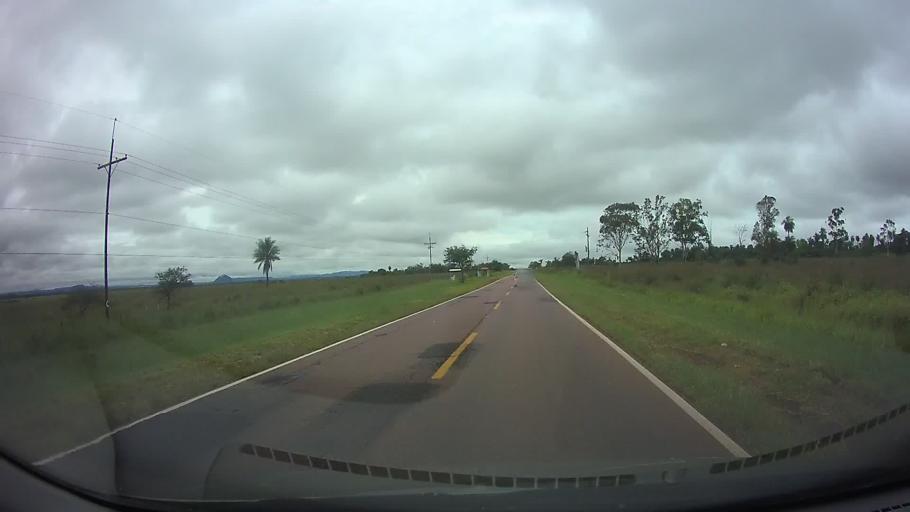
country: PY
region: Paraguari
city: Carapegua
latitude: -25.8141
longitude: -57.1771
